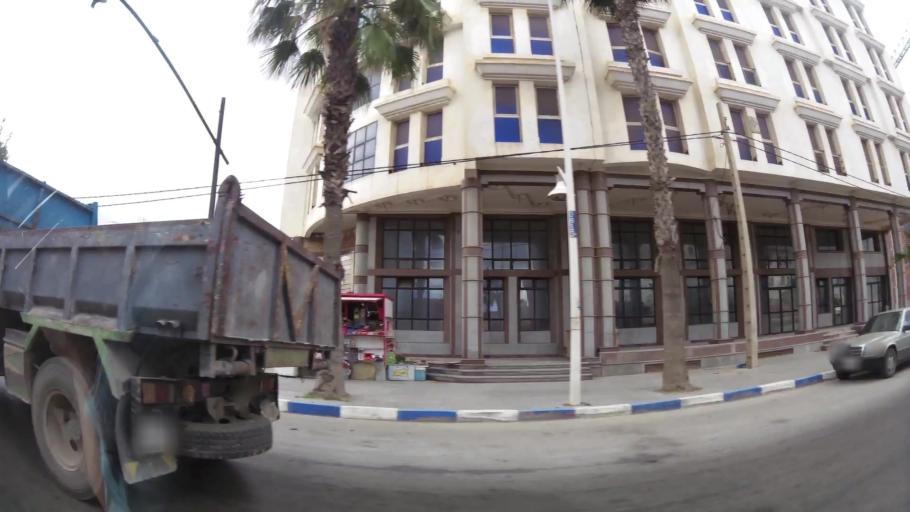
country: MA
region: Oriental
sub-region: Nador
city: Nador
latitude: 35.1586
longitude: -2.9303
